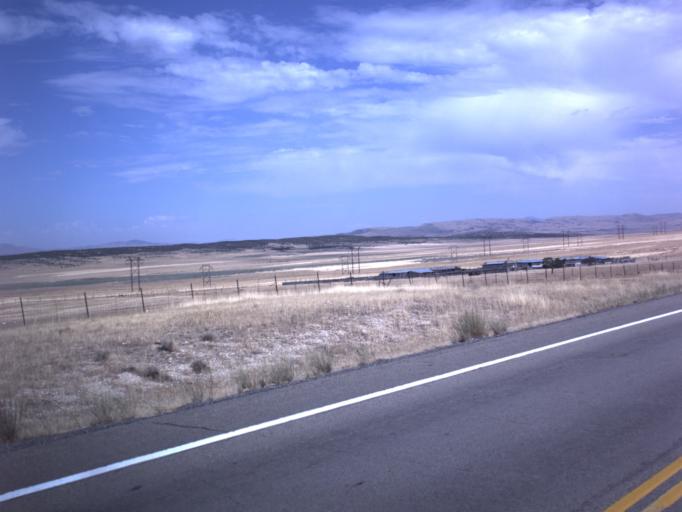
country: US
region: Utah
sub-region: Sanpete County
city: Gunnison
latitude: 39.4046
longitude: -111.9275
